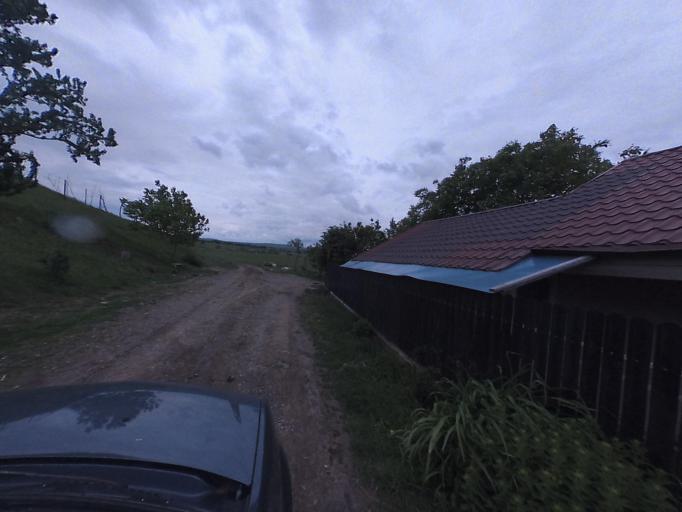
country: RO
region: Neamt
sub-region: Comuna Dulcesti
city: Dulcesti
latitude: 46.9638
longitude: 26.7808
